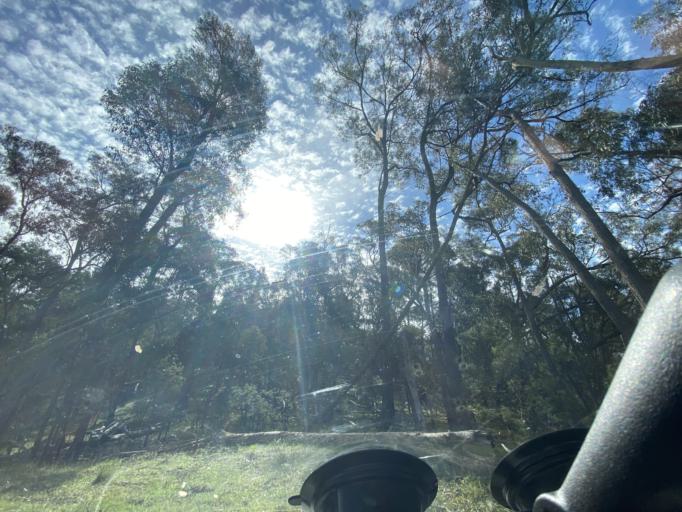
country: AU
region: Victoria
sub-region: Mansfield
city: Mansfield
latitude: -36.8114
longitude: 146.1158
